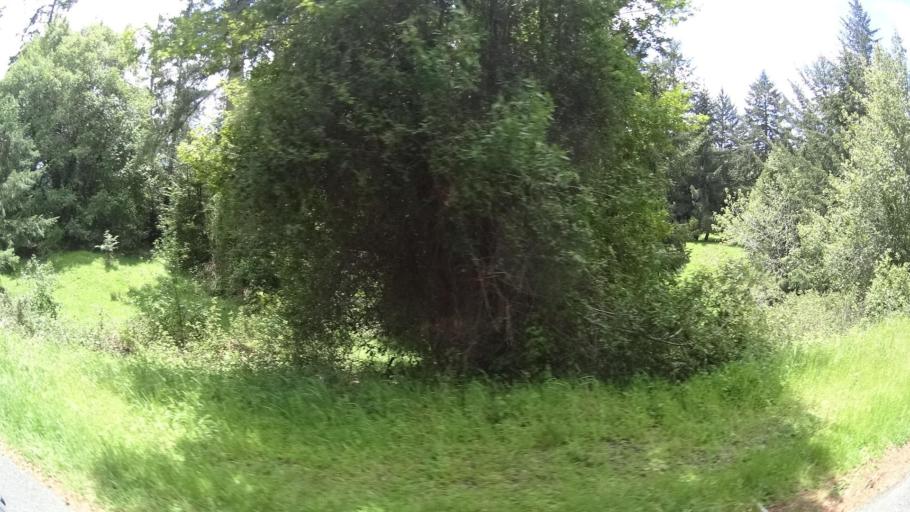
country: US
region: California
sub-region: Humboldt County
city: Blue Lake
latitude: 40.8450
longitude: -123.9120
